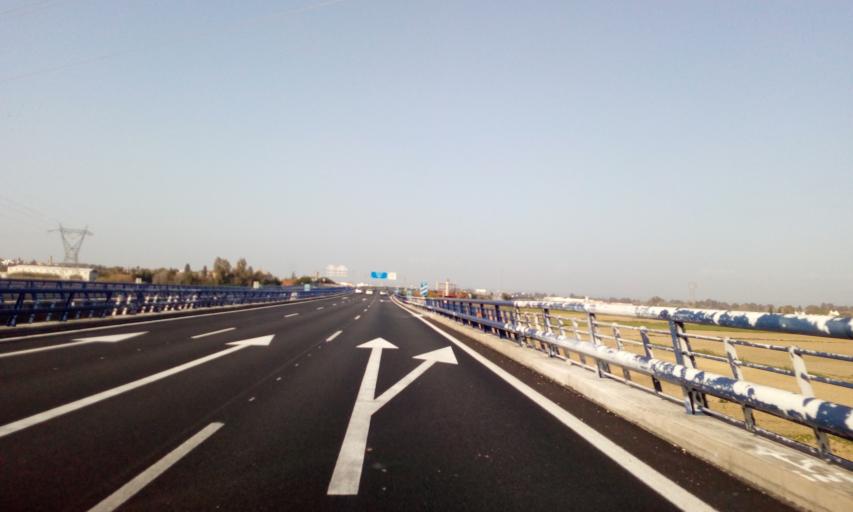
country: ES
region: Andalusia
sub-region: Provincia de Sevilla
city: Santiponce
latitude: 37.4250
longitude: -6.0292
